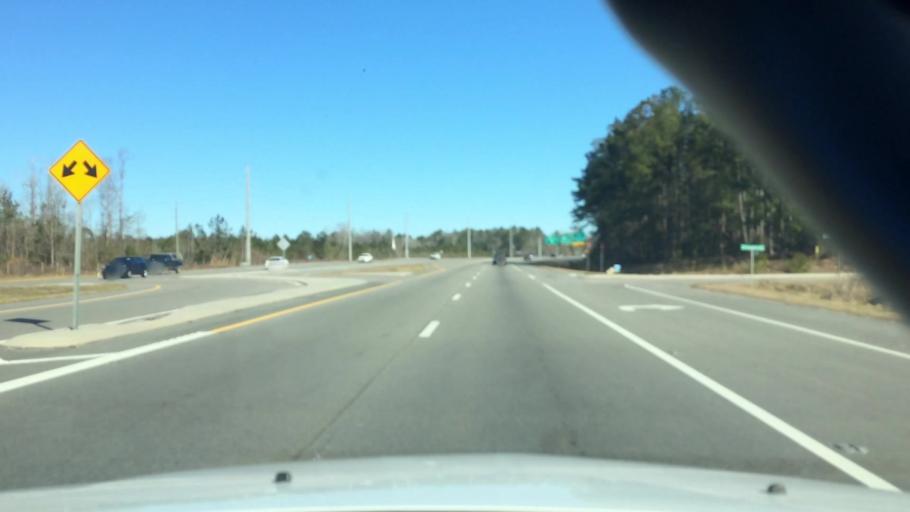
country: US
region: North Carolina
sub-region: Brunswick County
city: Leland
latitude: 34.1749
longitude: -78.0867
